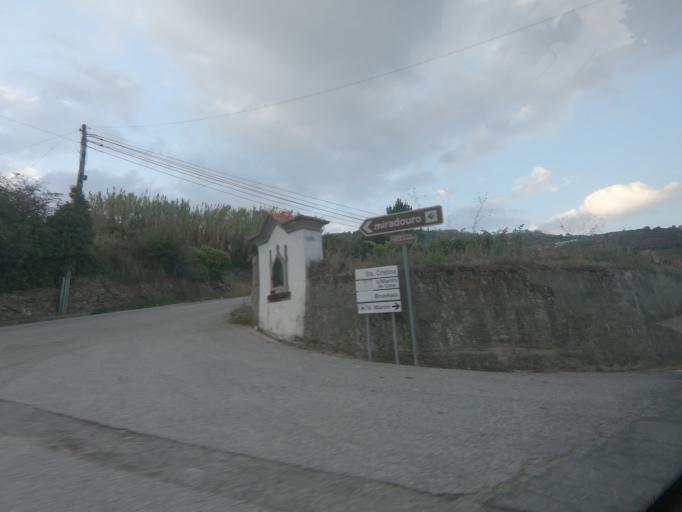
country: PT
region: Vila Real
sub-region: Mesao Frio
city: Mesao Frio
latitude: 41.1639
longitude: -7.8817
